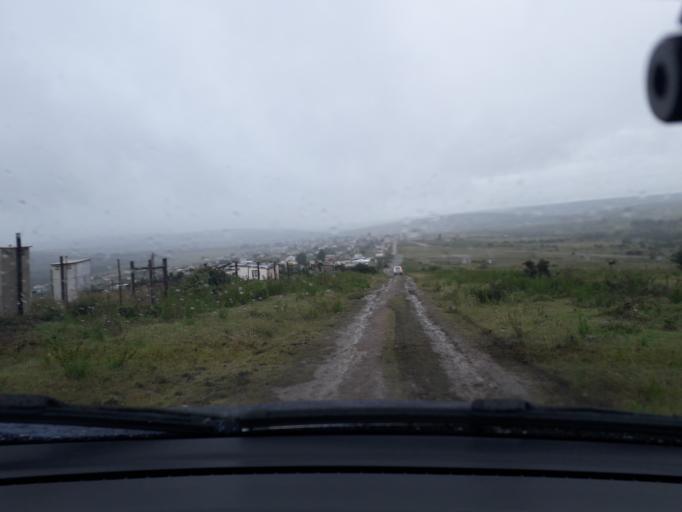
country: ZA
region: Eastern Cape
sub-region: Buffalo City Metropolitan Municipality
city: Bhisho
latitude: -32.8043
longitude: 27.3632
